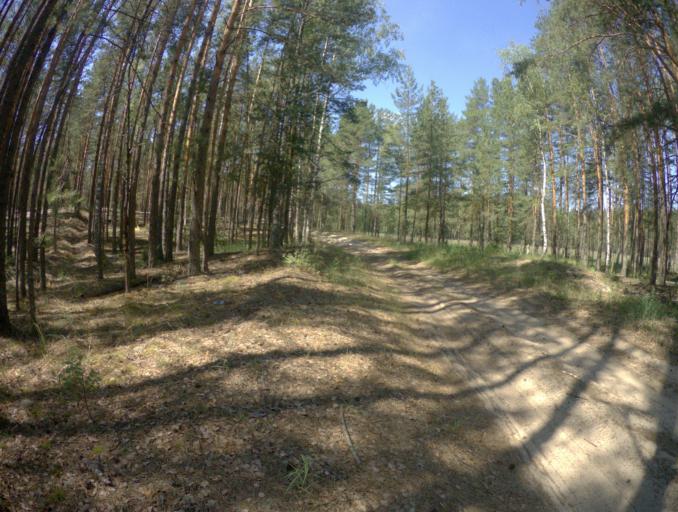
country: RU
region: Ivanovo
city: Talitsy
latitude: 56.3839
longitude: 42.3281
